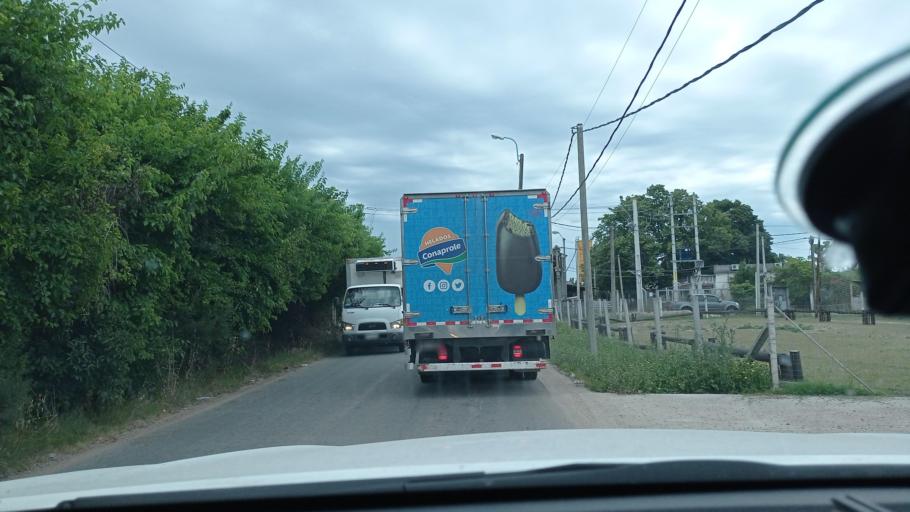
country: UY
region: Canelones
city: La Paz
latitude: -34.8104
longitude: -56.1937
